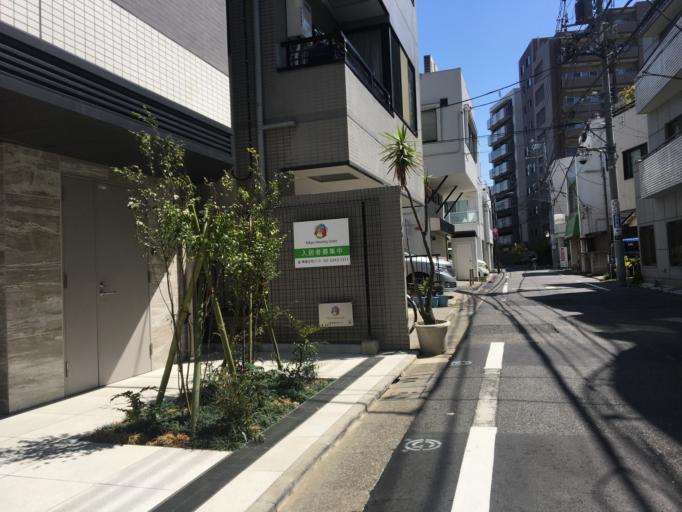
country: JP
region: Tokyo
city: Tokyo
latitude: 35.7311
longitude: 139.7361
